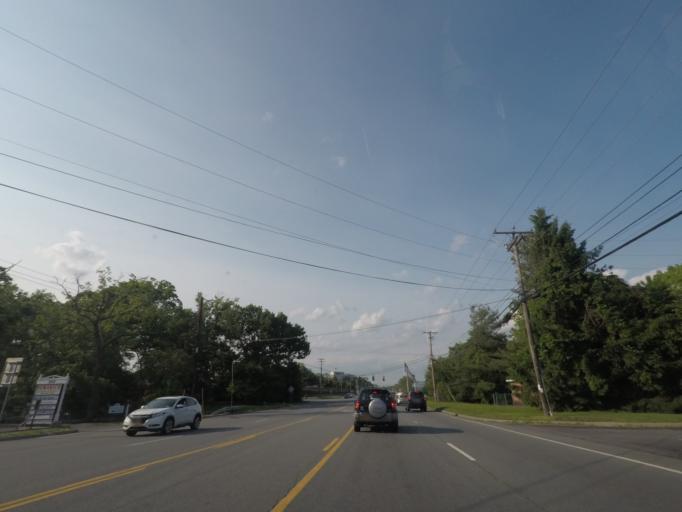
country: US
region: New York
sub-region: Orange County
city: Gardnertown
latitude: 41.5012
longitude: -74.0704
